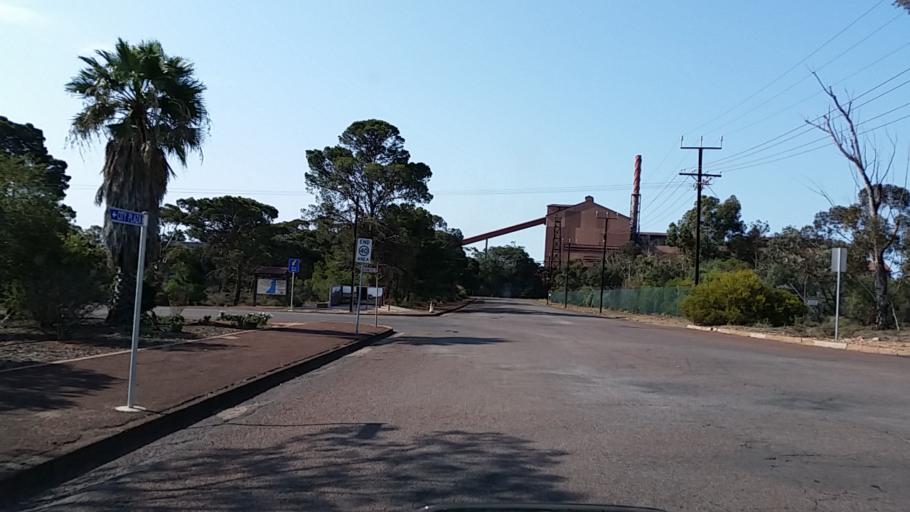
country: AU
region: South Australia
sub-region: Whyalla
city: Whyalla
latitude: -33.0351
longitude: 137.5879
